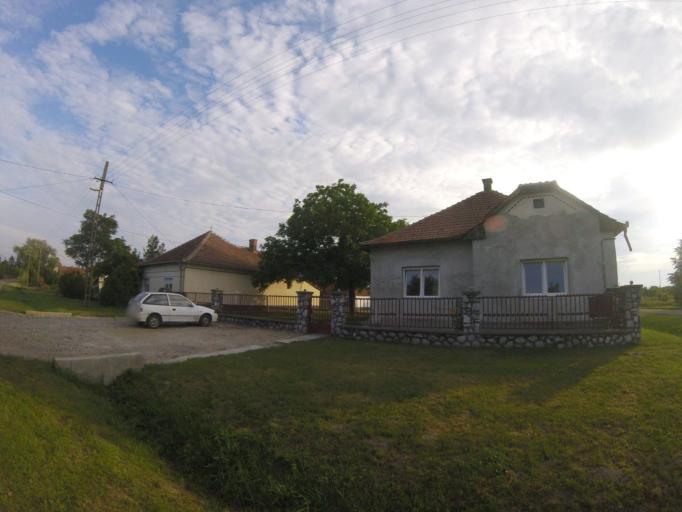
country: HU
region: Heves
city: Tiszanana
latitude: 47.5991
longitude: 20.5867
